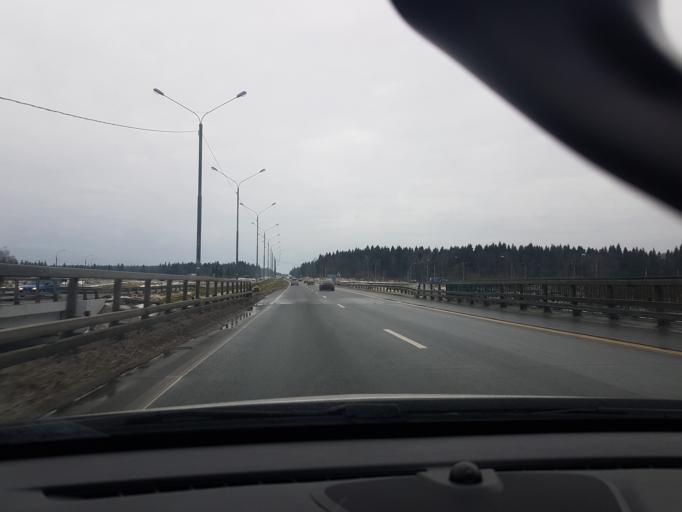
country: RU
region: Moskovskaya
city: Sychevo
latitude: 55.9849
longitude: 36.3393
